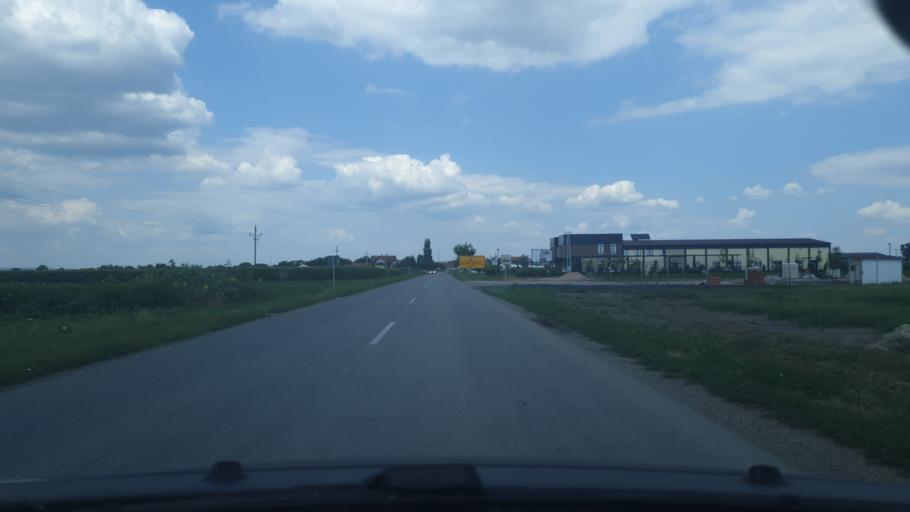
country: RS
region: Autonomna Pokrajina Vojvodina
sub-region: Sremski Okrug
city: Pecinci
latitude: 44.8938
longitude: 19.9653
